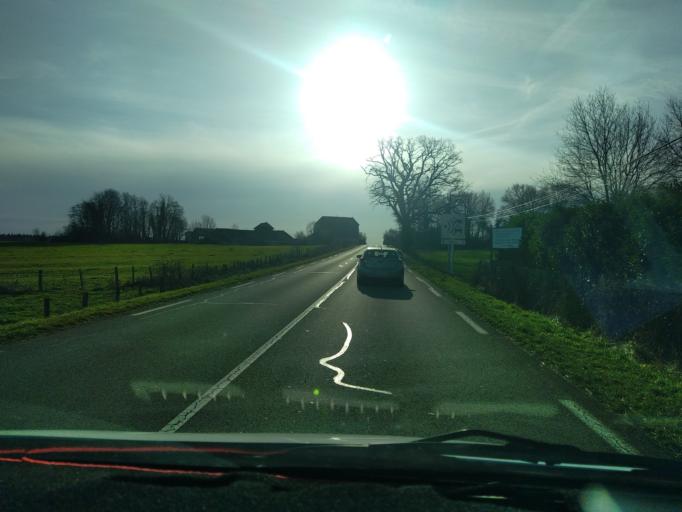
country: FR
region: Franche-Comte
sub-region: Departement de la Haute-Saone
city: Gray
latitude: 47.3753
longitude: 5.6639
